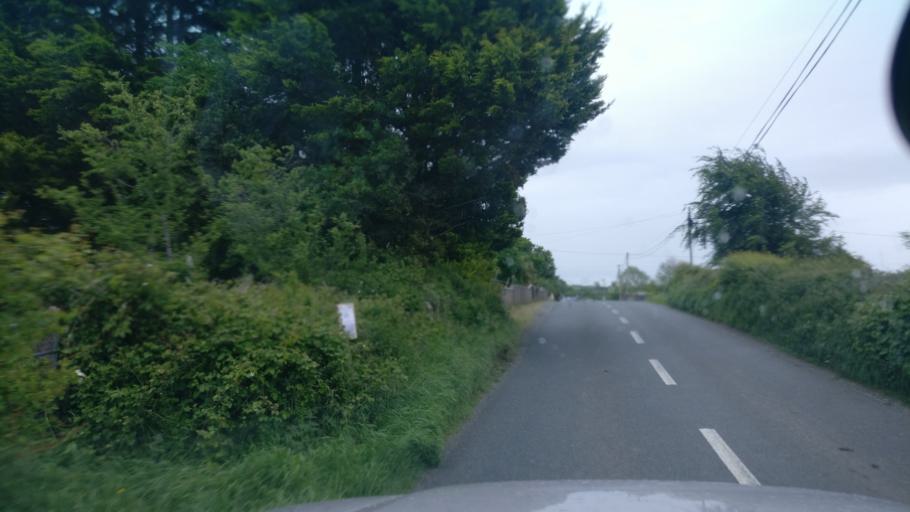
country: IE
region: Connaught
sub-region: County Galway
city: Gort
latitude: 53.0658
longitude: -8.7755
